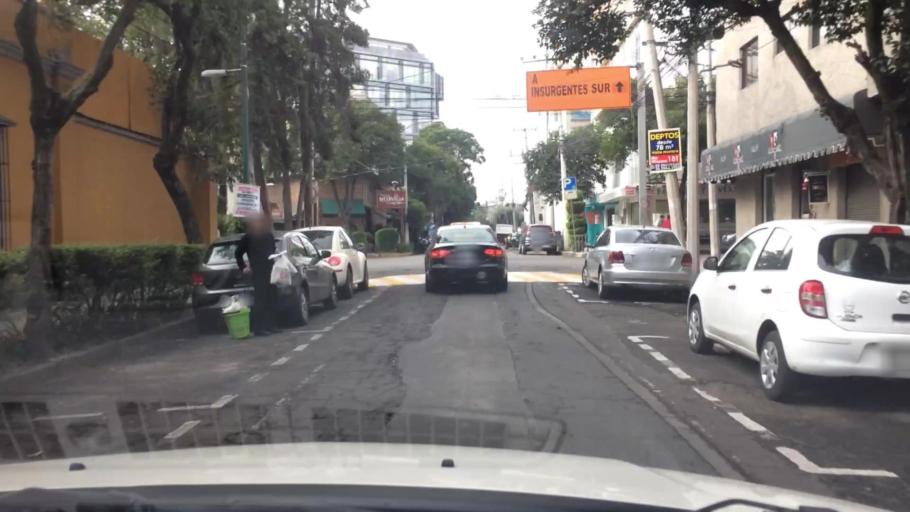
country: MX
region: Mexico City
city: Alvaro Obregon
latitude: 19.3648
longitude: -99.1878
